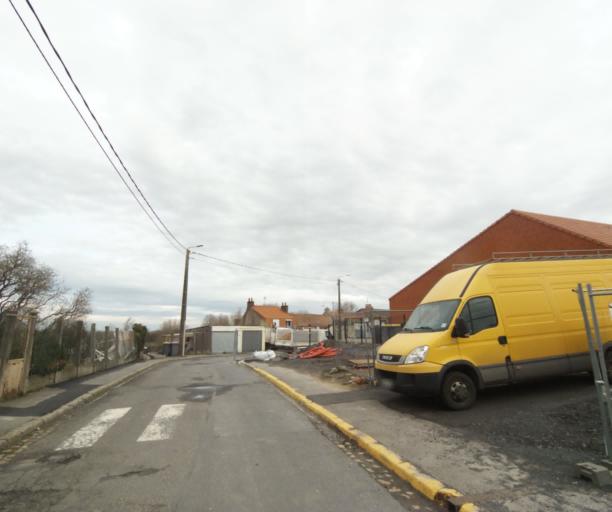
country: BE
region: Wallonia
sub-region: Province du Hainaut
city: Peruwelz
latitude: 50.4885
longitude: 3.5798
